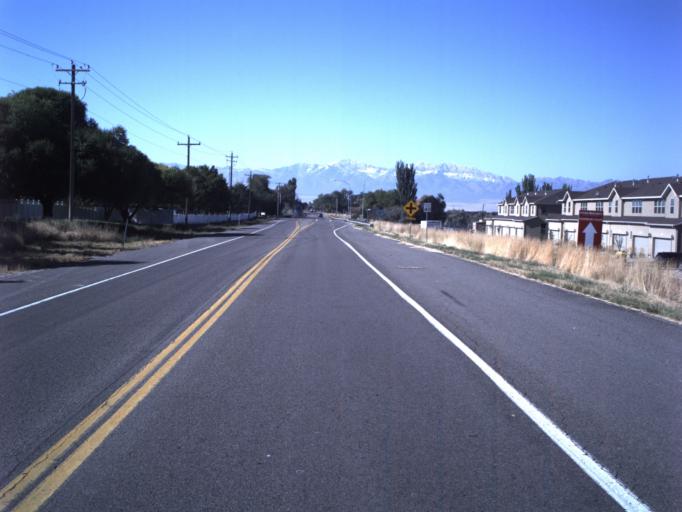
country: US
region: Utah
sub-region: Tooele County
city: Stansbury park
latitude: 40.6524
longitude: -112.2938
